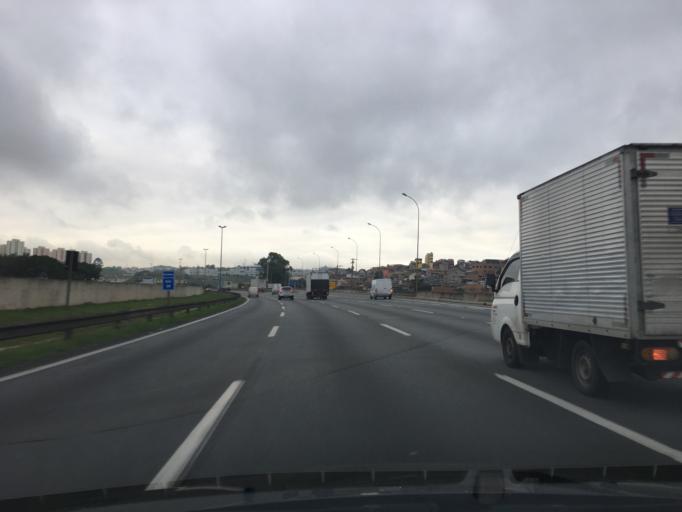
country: BR
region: Sao Paulo
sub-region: Carapicuiba
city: Carapicuiba
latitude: -23.5476
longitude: -46.8204
